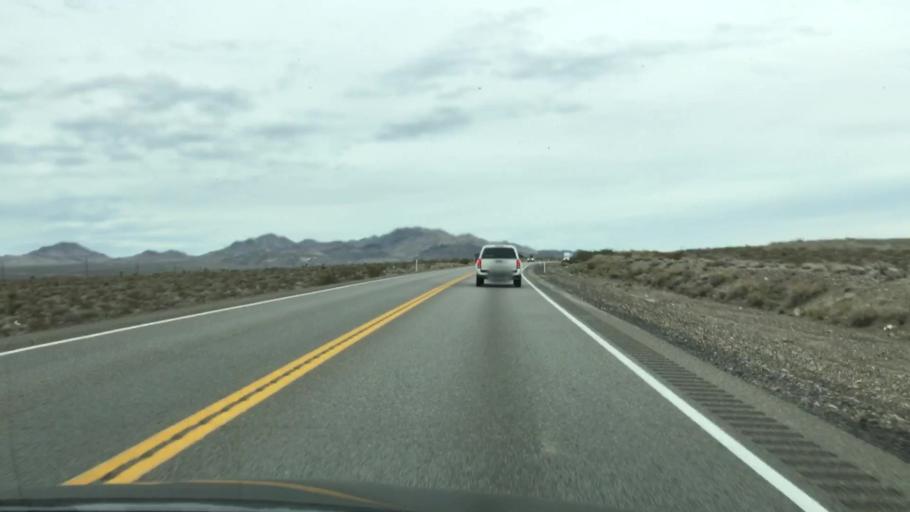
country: US
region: Nevada
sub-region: Nye County
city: Pahrump
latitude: 36.5872
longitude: -116.0552
